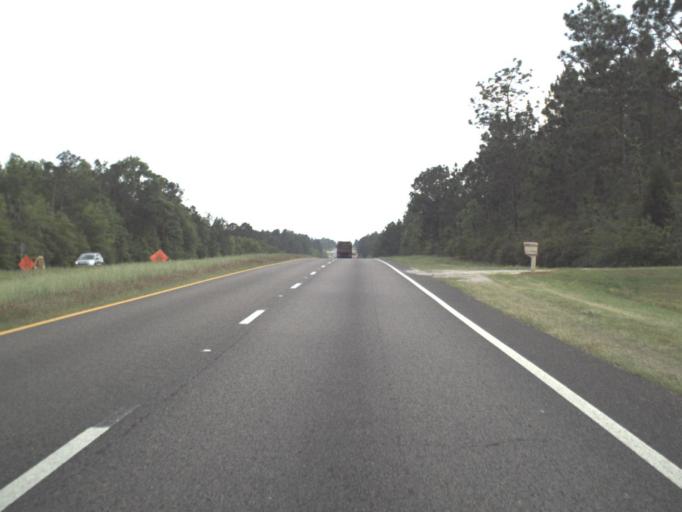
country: US
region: Florida
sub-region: Escambia County
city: Molino
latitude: 30.6955
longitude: -87.3508
